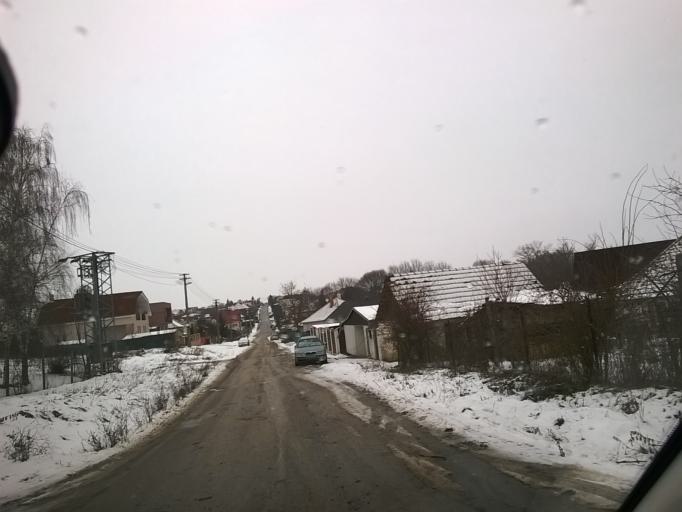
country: SK
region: Nitriansky
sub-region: Okres Nitra
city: Nitra
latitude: 48.2813
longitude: 18.0134
